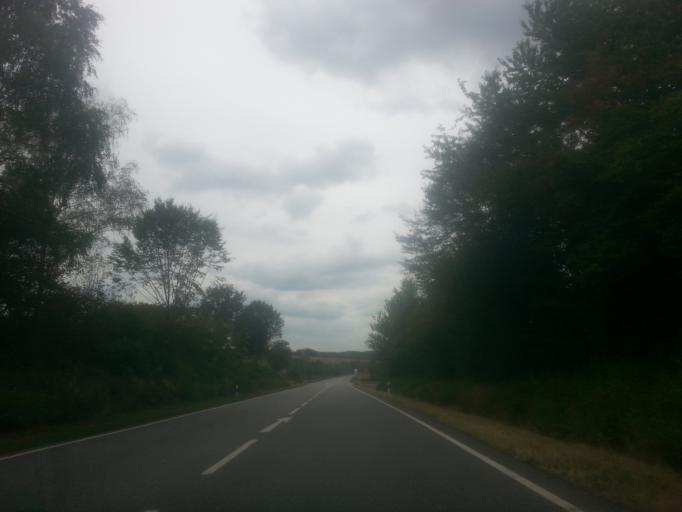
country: DE
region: Bavaria
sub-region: Lower Bavaria
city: Pfeffenhausen
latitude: 48.6687
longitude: 11.9433
